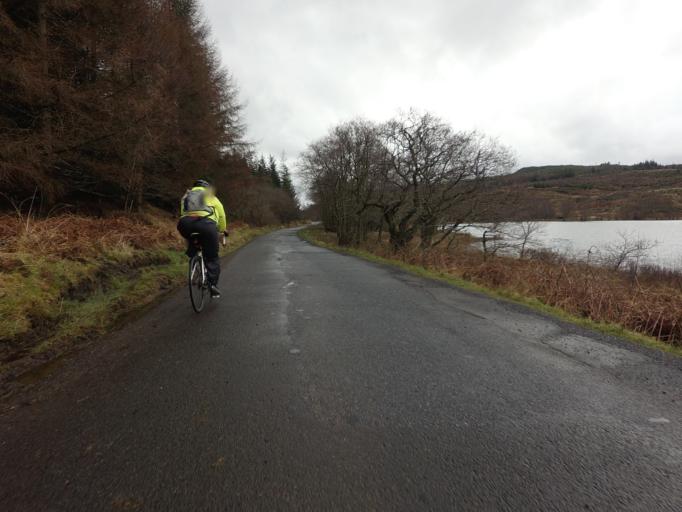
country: GB
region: Scotland
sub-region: West Dunbartonshire
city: Balloch
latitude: 56.2020
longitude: -4.5292
